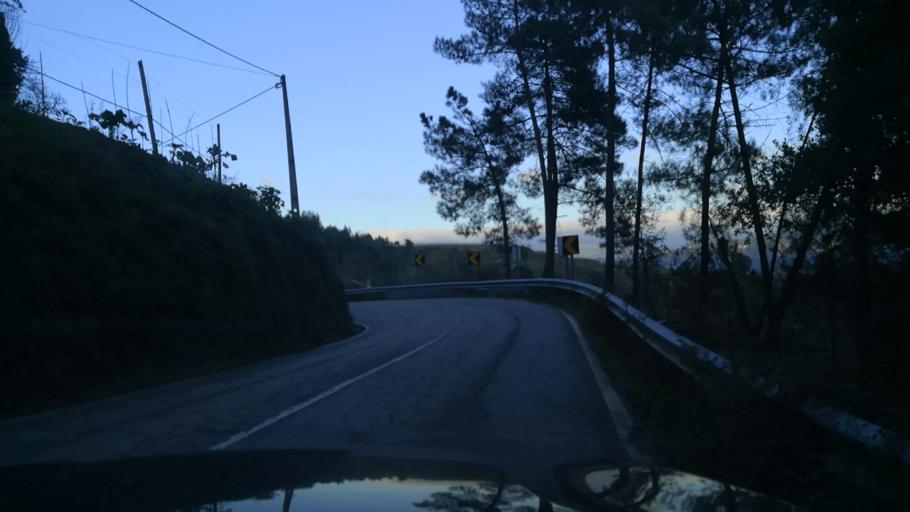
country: PT
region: Vila Real
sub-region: Mondim de Basto
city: Mondim de Basto
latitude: 41.4609
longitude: -7.9631
